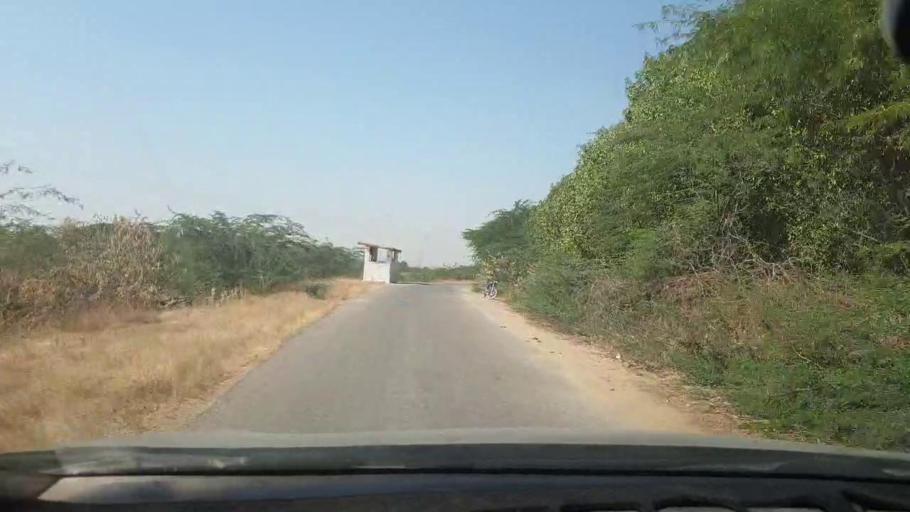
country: PK
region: Sindh
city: Malir Cantonment
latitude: 25.1618
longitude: 67.1557
